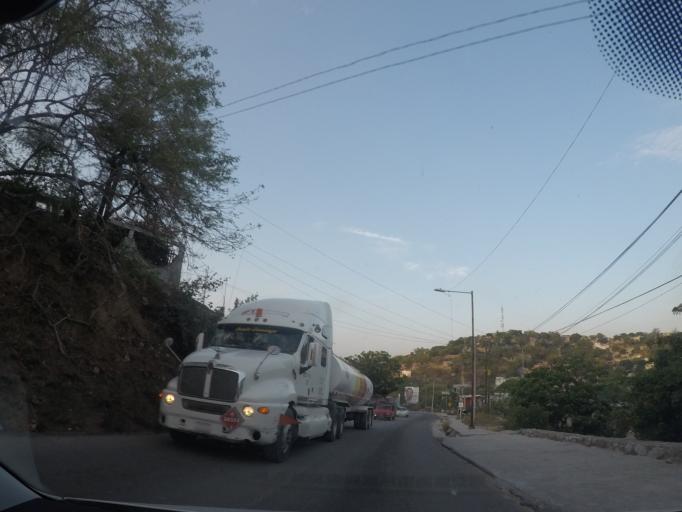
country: MX
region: Oaxaca
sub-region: Salina Cruz
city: Salina Cruz
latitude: 16.1946
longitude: -95.2045
